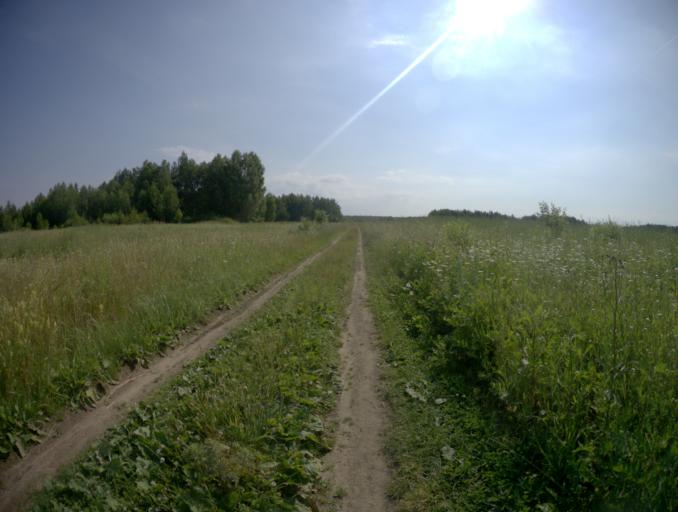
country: RU
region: Vladimir
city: Vyazniki
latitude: 56.3383
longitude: 42.1382
